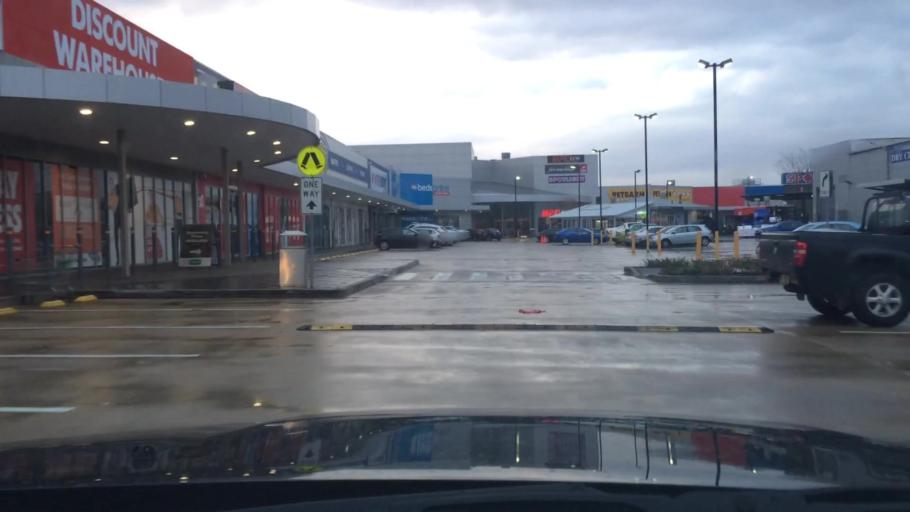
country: AU
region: New South Wales
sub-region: Fairfield
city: Fairfield Heights
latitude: -33.8506
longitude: 150.8974
